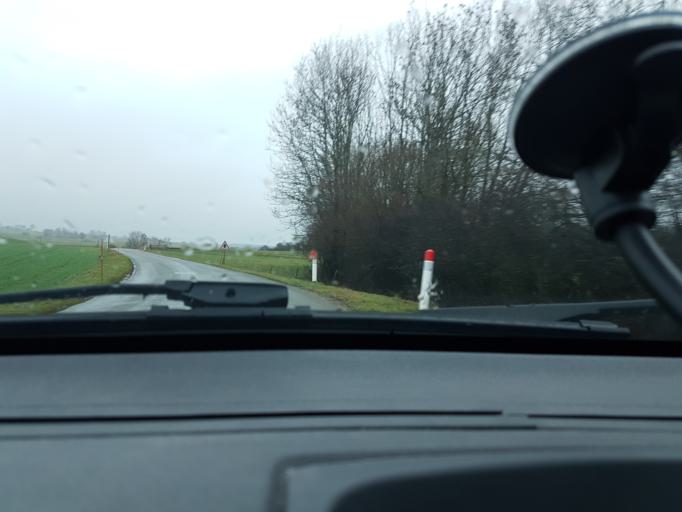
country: FR
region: Franche-Comte
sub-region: Departement du Doubs
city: Valdahon
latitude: 47.1057
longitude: 6.3591
